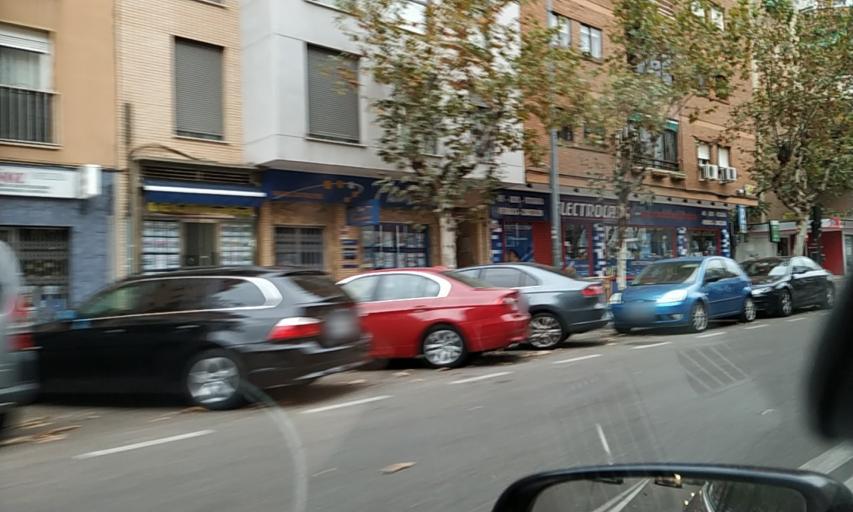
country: ES
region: Extremadura
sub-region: Provincia de Badajoz
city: Badajoz
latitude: 38.8792
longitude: -6.9597
